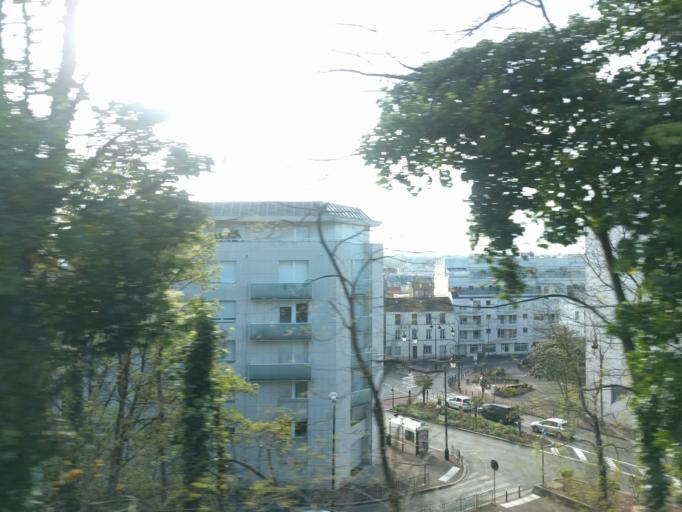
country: FR
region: Ile-de-France
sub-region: Departement des Hauts-de-Seine
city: Suresnes
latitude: 48.8802
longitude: 2.2306
